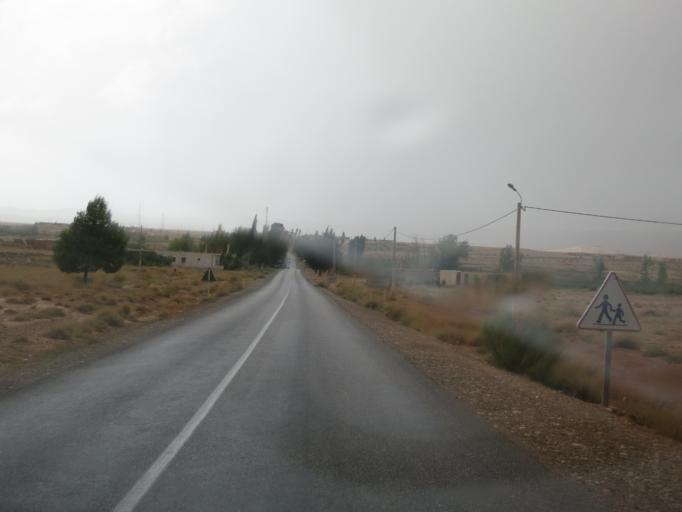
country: MA
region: Meknes-Tafilalet
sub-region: Khenifra
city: Itzer
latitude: 32.8778
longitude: -4.9471
